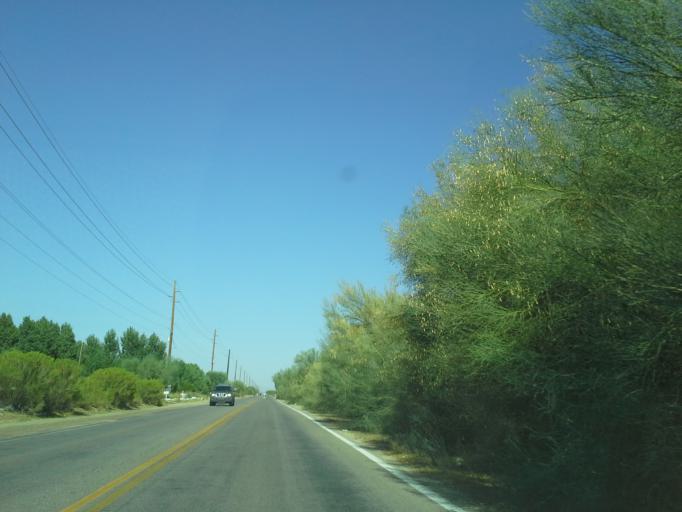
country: US
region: Arizona
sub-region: Maricopa County
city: Queen Creek
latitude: 33.2046
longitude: -111.6817
